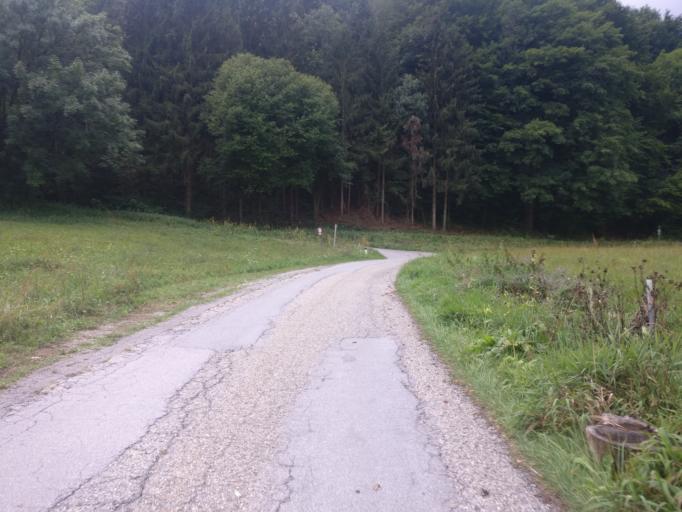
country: AT
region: Styria
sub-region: Politischer Bezirk Graz-Umgebung
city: Frohnleiten
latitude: 47.2311
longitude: 15.3183
